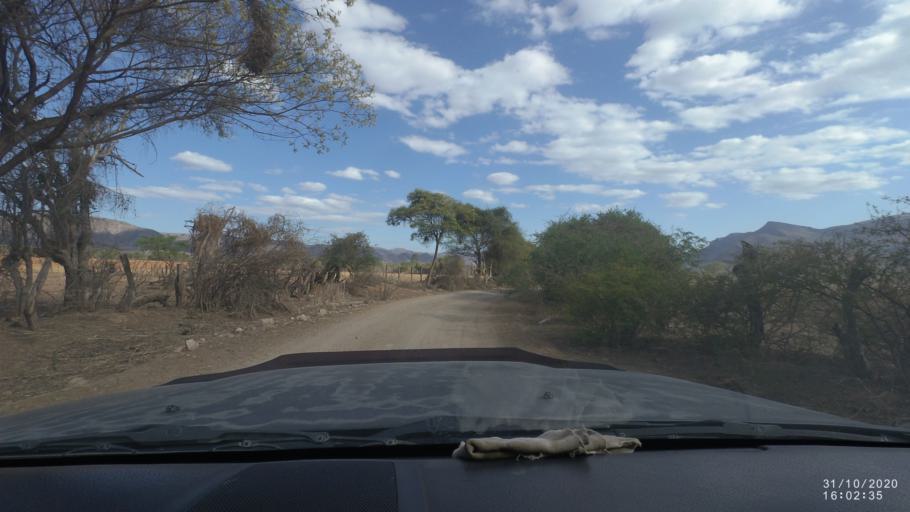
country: BO
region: Chuquisaca
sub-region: Provincia Zudanez
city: Mojocoya
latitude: -18.3478
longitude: -64.6565
